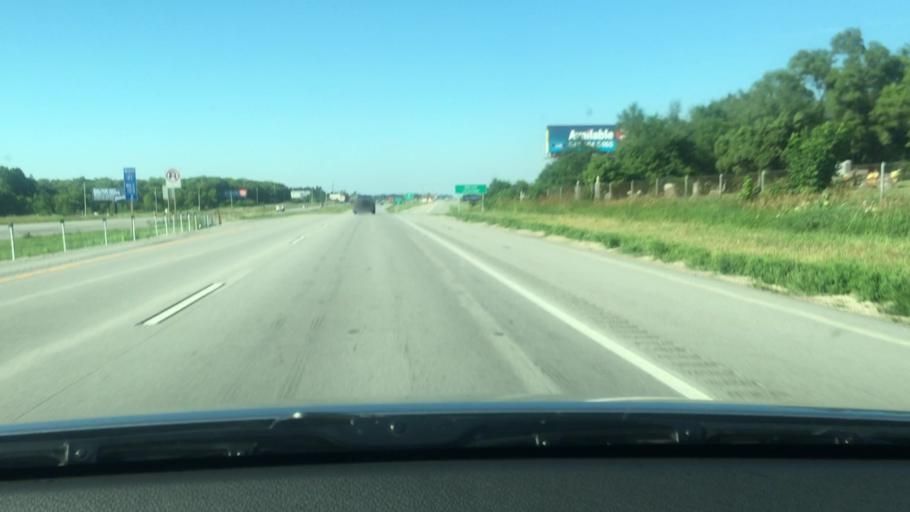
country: US
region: Wisconsin
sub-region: Brown County
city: Wrightstown
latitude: 44.3360
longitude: -88.2044
